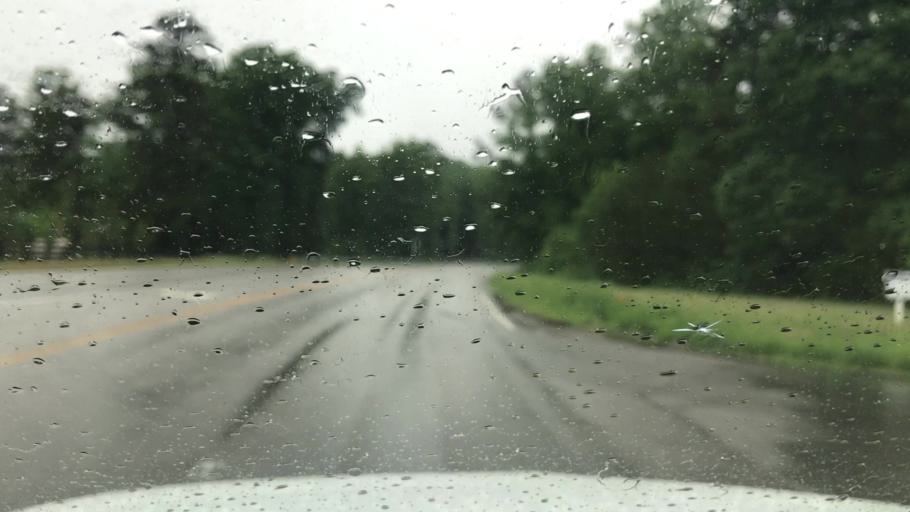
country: US
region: Virginia
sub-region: Hanover County
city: Ashland
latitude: 37.8195
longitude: -77.4742
